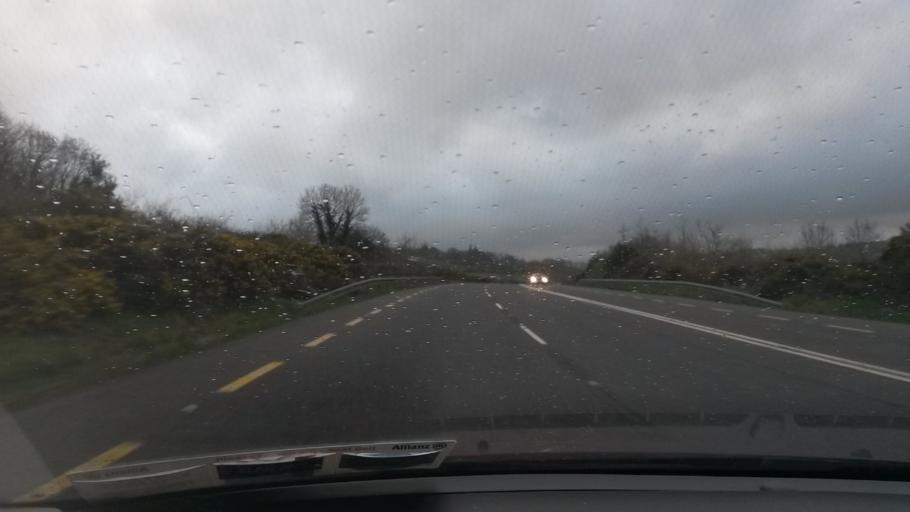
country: IE
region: Munster
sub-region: County Limerick
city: Abbeyfeale
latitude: 52.3486
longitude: -9.3335
